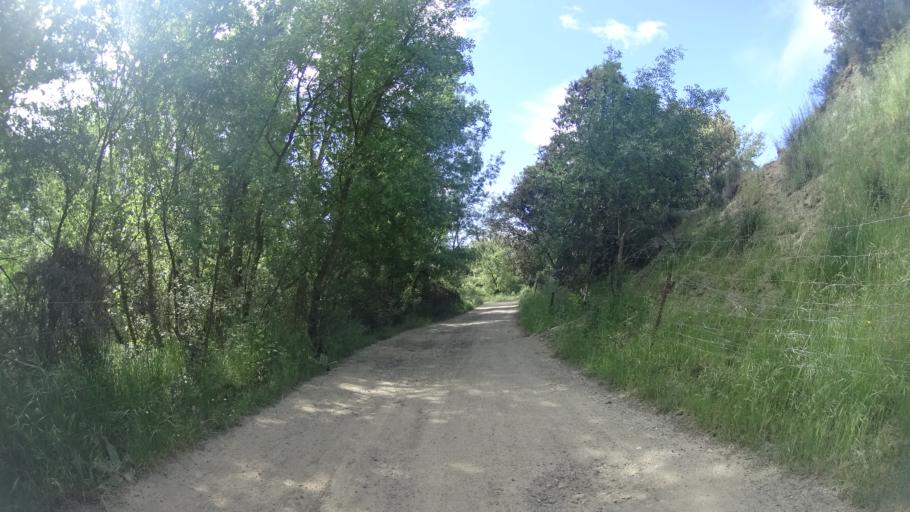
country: ES
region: Madrid
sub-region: Provincia de Madrid
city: Brunete
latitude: 40.4263
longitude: -3.9528
